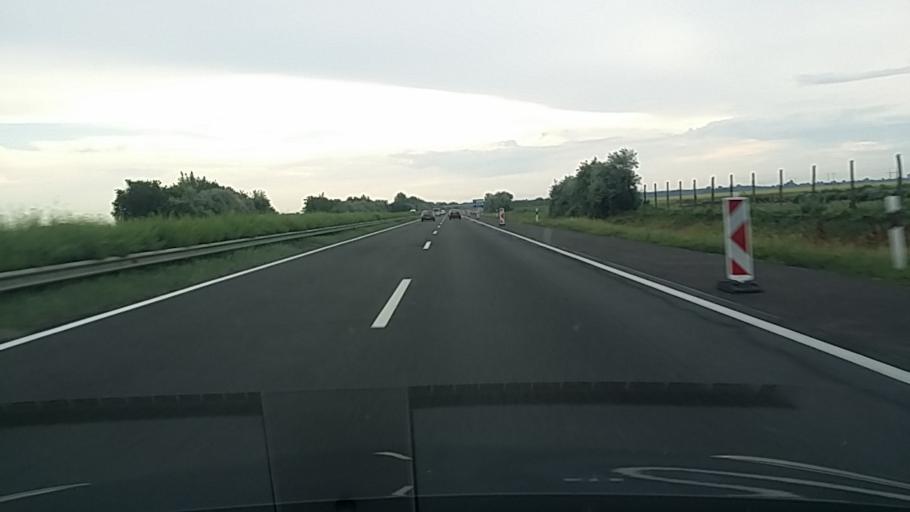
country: HU
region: Heves
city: Erdotelek
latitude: 47.7265
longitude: 20.3420
